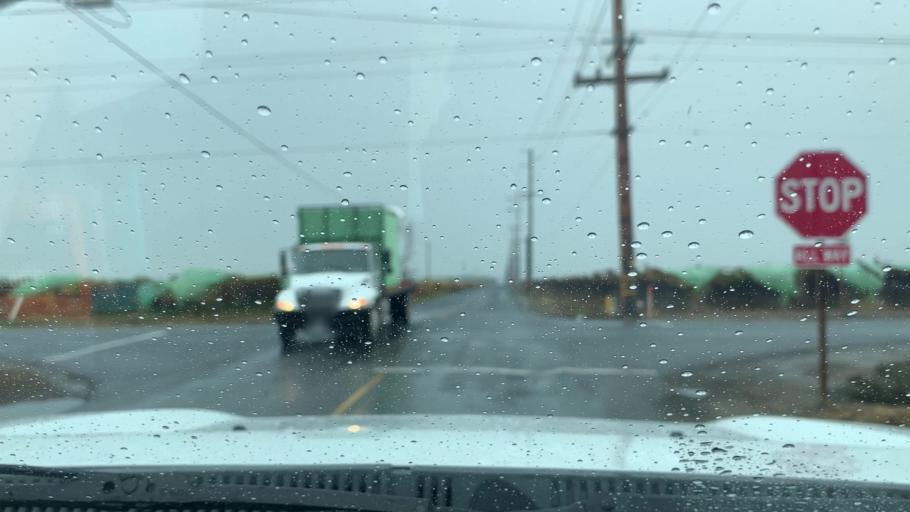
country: US
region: California
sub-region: Tulare County
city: Earlimart
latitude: 35.8339
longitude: -119.2504
